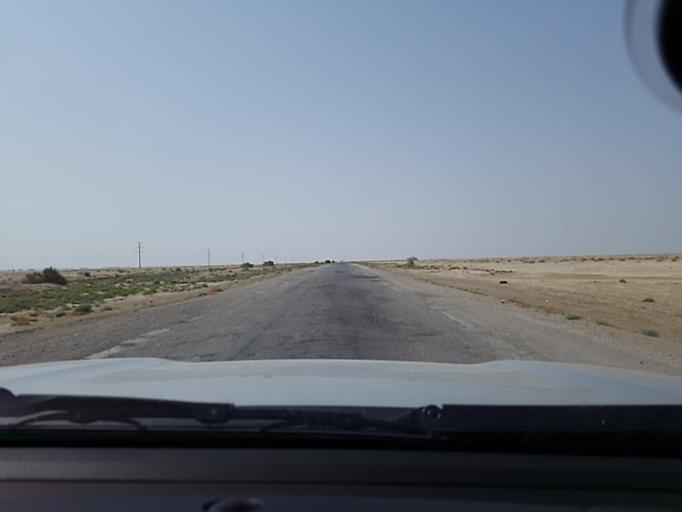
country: TM
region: Balkan
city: Gumdag
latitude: 38.8858
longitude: 54.5932
